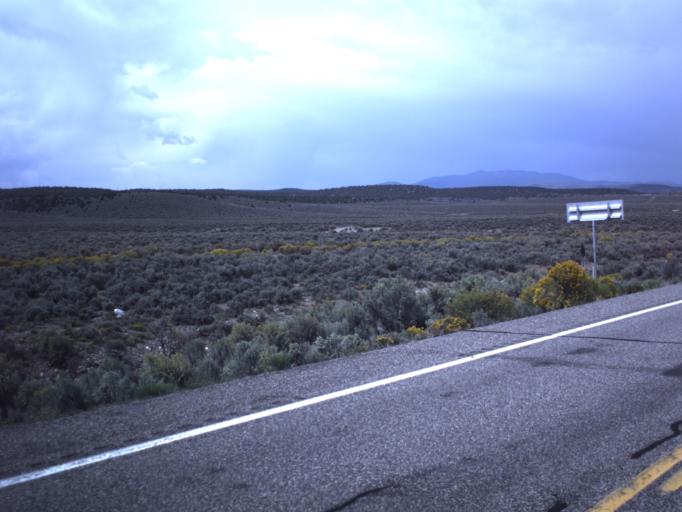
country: US
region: Utah
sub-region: Garfield County
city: Panguitch
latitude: 37.9692
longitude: -112.4103
